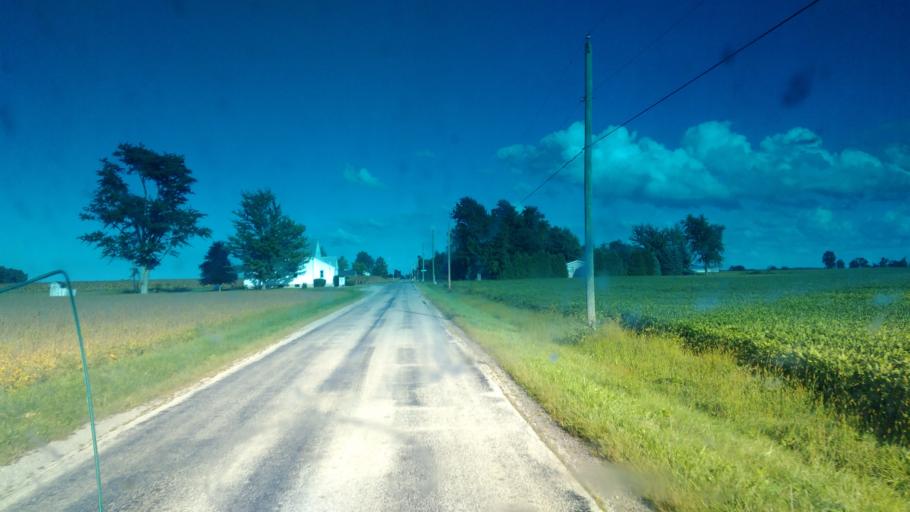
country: US
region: Ohio
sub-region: Hancock County
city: Arlington
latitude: 40.9356
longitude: -83.6251
